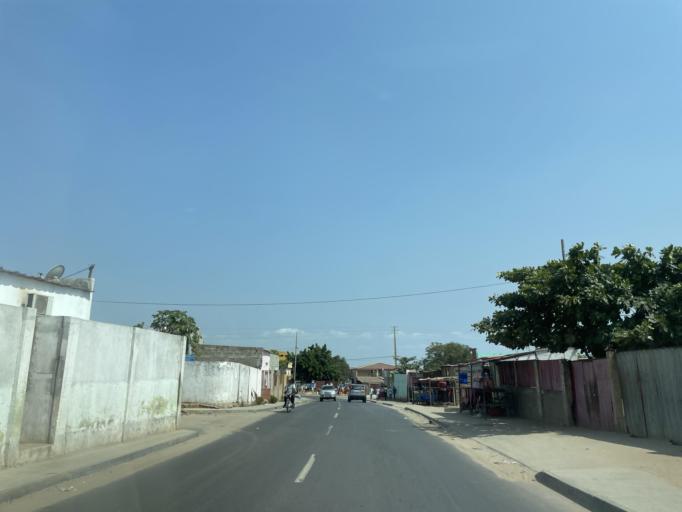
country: AO
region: Luanda
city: Luanda
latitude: -8.9320
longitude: 13.2047
